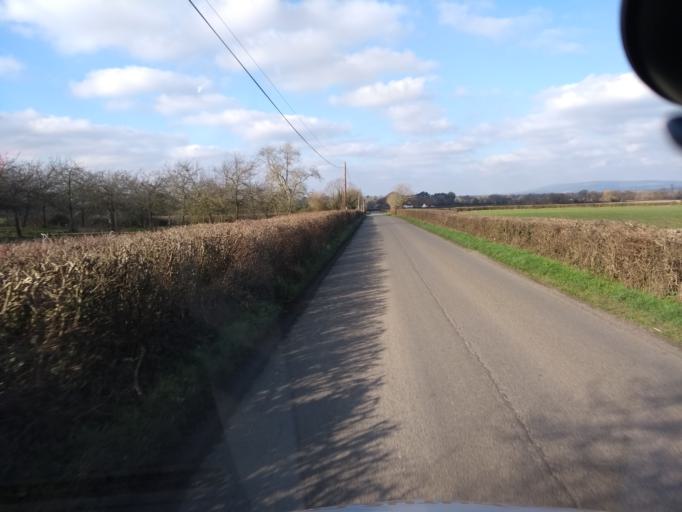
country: GB
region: England
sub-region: Somerset
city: Creech Saint Michael
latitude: 50.9835
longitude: -3.0612
